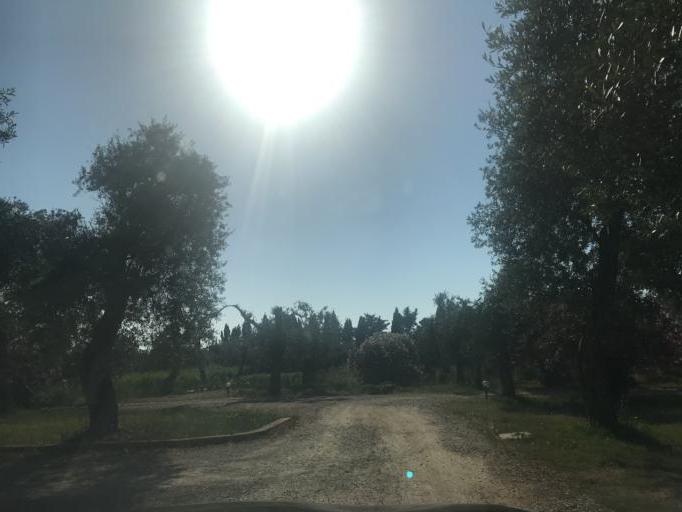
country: IT
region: Sardinia
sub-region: Provincia di Sassari
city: Alghero
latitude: 40.5491
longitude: 8.3467
